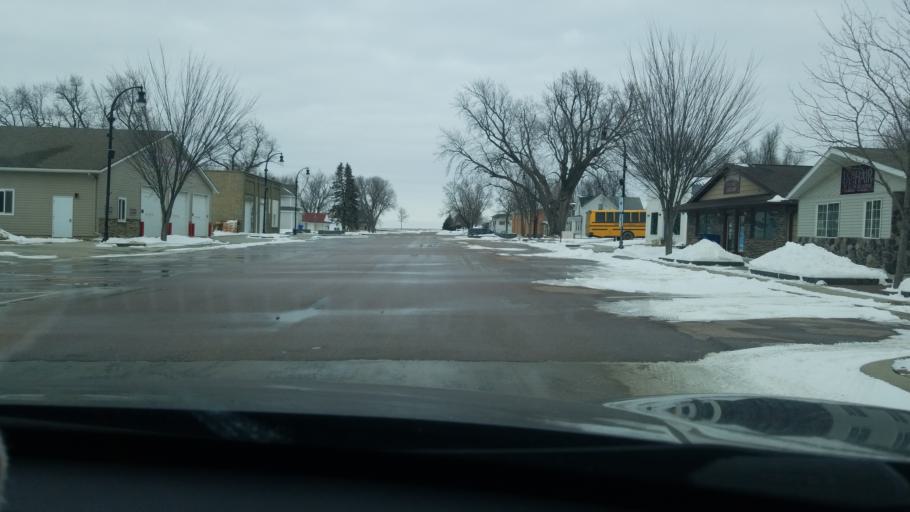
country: US
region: South Dakota
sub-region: Minnehaha County
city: Brandon
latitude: 43.4539
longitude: -96.4342
